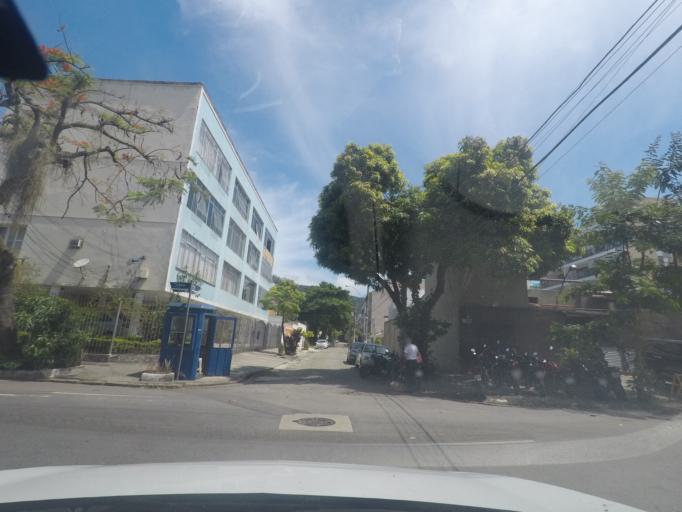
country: BR
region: Rio de Janeiro
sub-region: Niteroi
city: Niteroi
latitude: -22.9162
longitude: -43.0939
